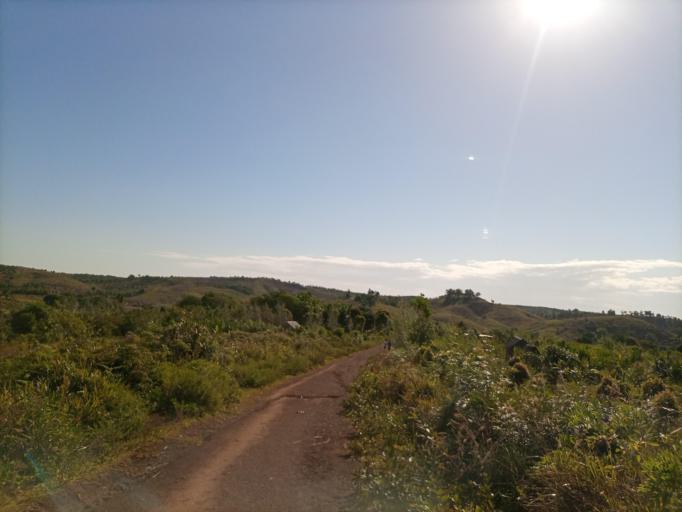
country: MG
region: Atsimo-Atsinanana
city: Vohipaho
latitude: -23.6056
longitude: 47.5181
